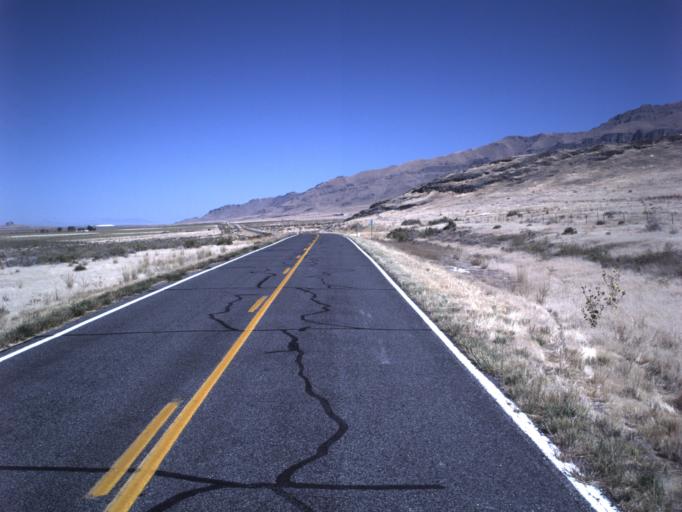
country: US
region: Utah
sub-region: Tooele County
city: Grantsville
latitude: 40.6086
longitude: -112.7074
